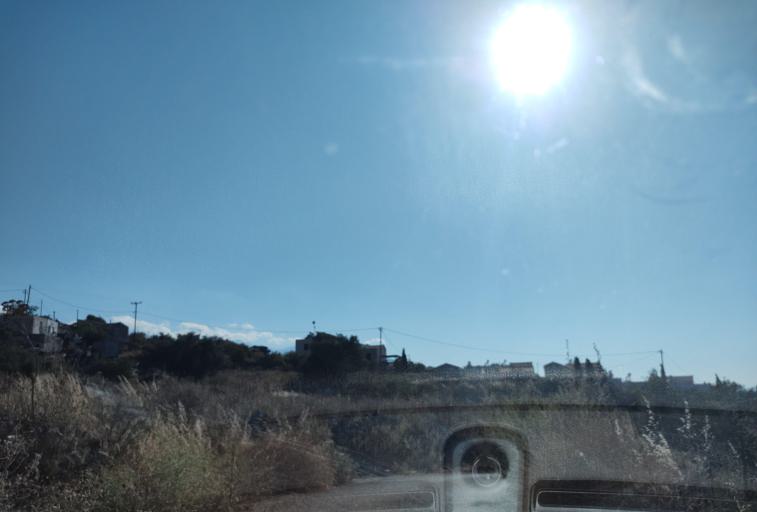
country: GR
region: Crete
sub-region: Nomos Chanias
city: Georgioupolis
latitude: 35.3968
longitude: 24.2352
